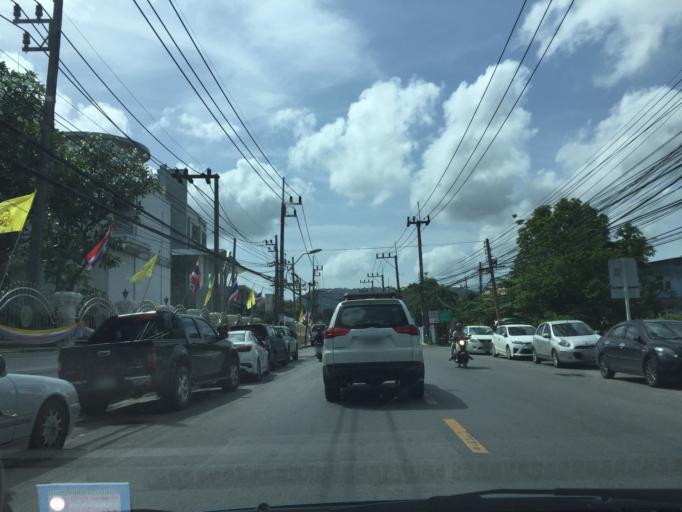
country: TH
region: Phuket
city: Wichit
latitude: 7.8975
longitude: 98.3839
